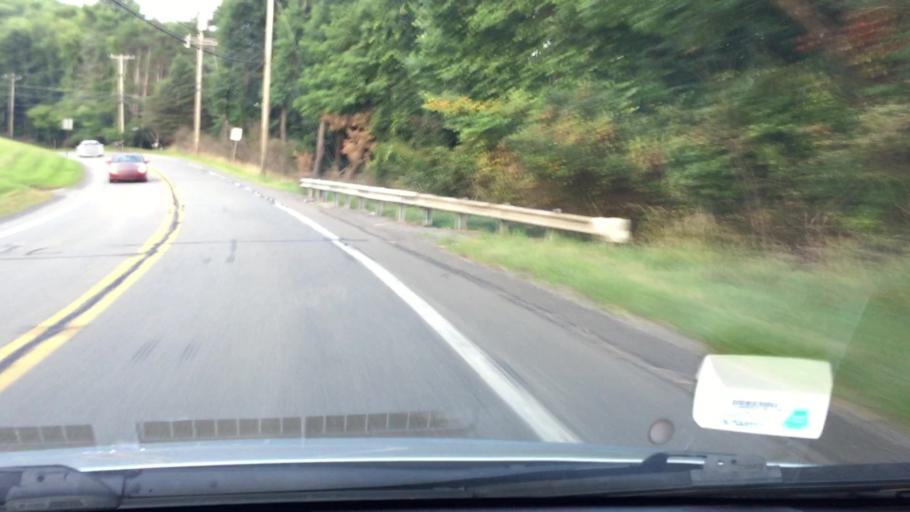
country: US
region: Pennsylvania
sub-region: Allegheny County
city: Gibsonia
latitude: 40.6296
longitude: -80.0119
